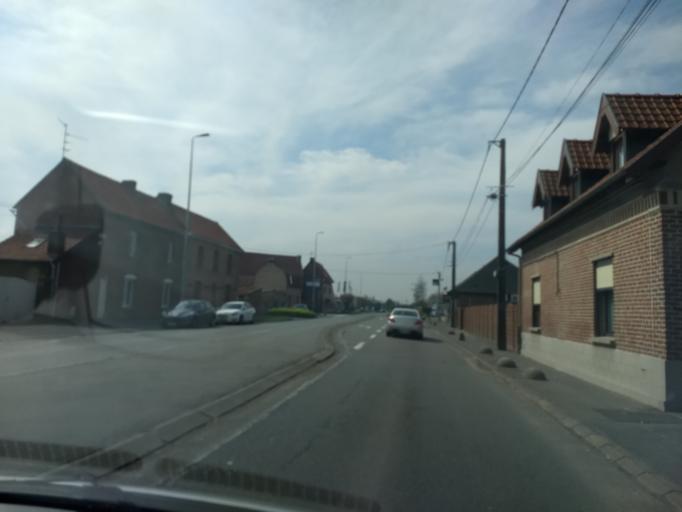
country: FR
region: Nord-Pas-de-Calais
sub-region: Departement du Pas-de-Calais
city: Biache-Saint-Vaast
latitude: 50.3345
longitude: 2.9302
